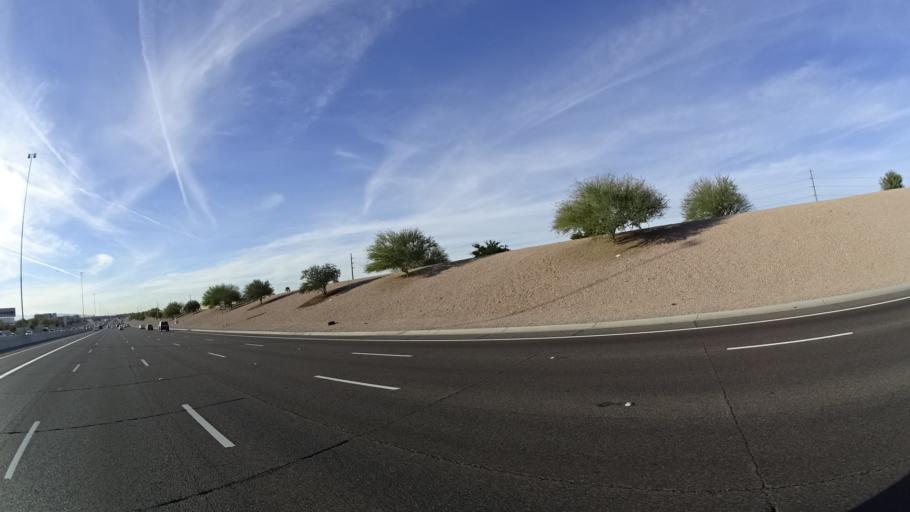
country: US
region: Arizona
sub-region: Maricopa County
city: Gilbert
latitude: 33.3863
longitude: -111.7072
